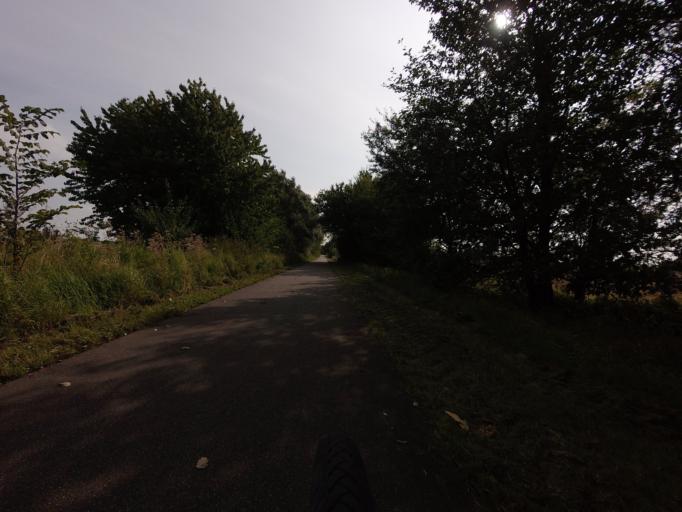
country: DK
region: Zealand
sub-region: Naestved Kommune
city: Naestved
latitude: 55.2550
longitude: 11.6783
